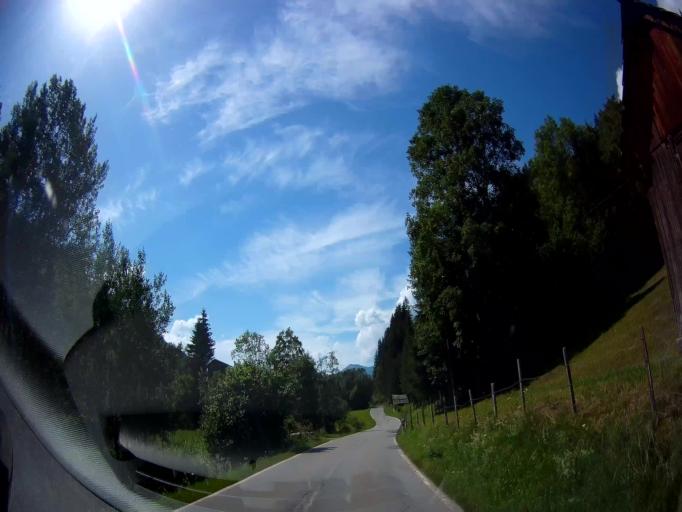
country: AT
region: Salzburg
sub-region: Politischer Bezirk Tamsweg
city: Thomatal
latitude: 47.0659
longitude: 13.7632
